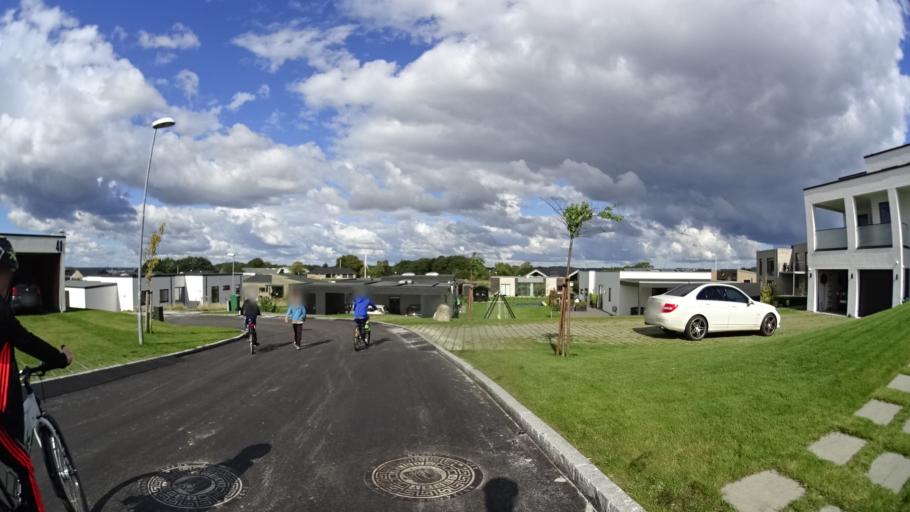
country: DK
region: Central Jutland
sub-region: Arhus Kommune
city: Stavtrup
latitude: 56.1310
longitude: 10.1035
